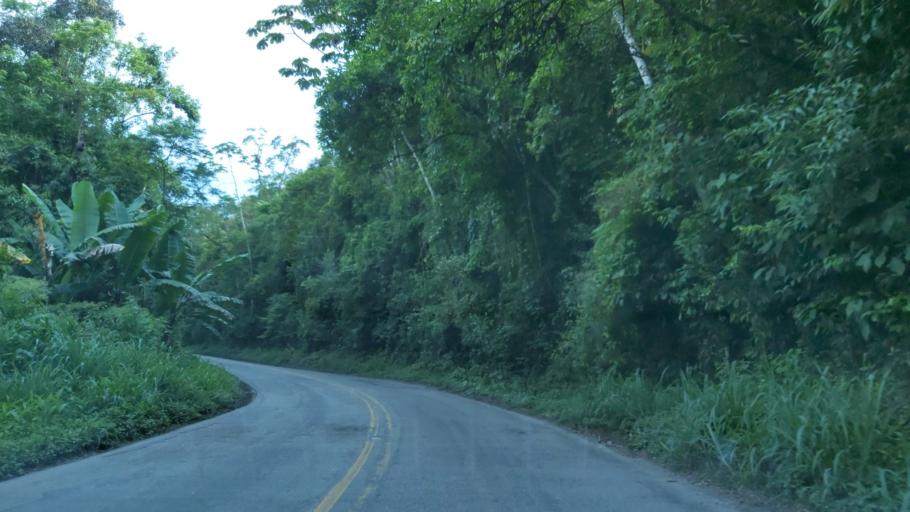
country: BR
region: Sao Paulo
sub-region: Miracatu
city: Miracatu
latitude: -24.0473
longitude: -47.5695
